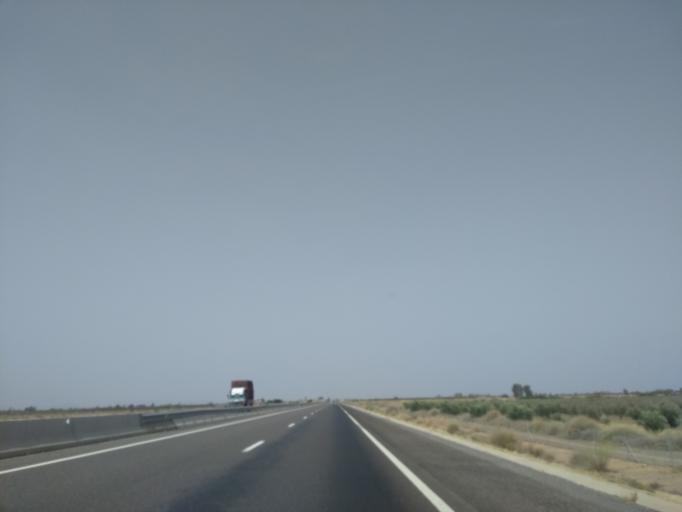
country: MA
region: Marrakech-Tensift-Al Haouz
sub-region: Marrakech
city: Marrakesh
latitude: 31.6136
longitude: -8.3820
